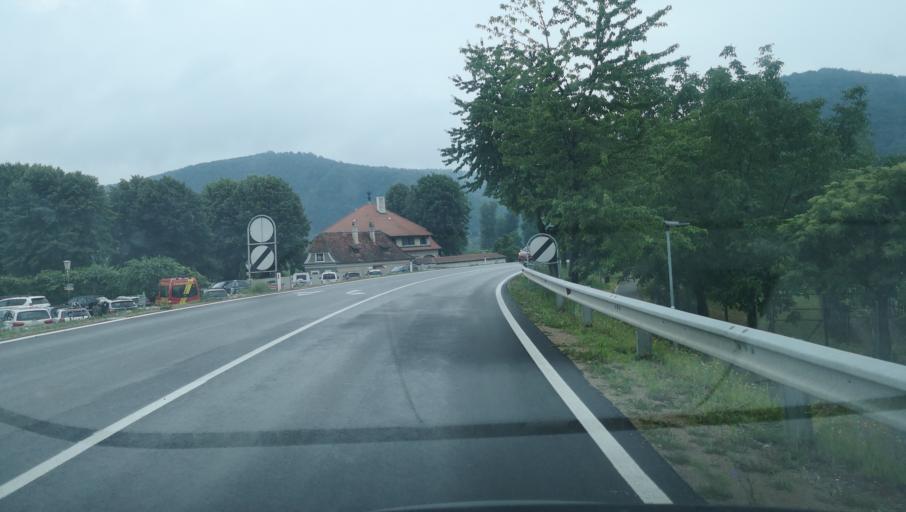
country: AT
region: Lower Austria
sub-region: Politischer Bezirk Krems
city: Durnstein
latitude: 48.3930
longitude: 15.5234
